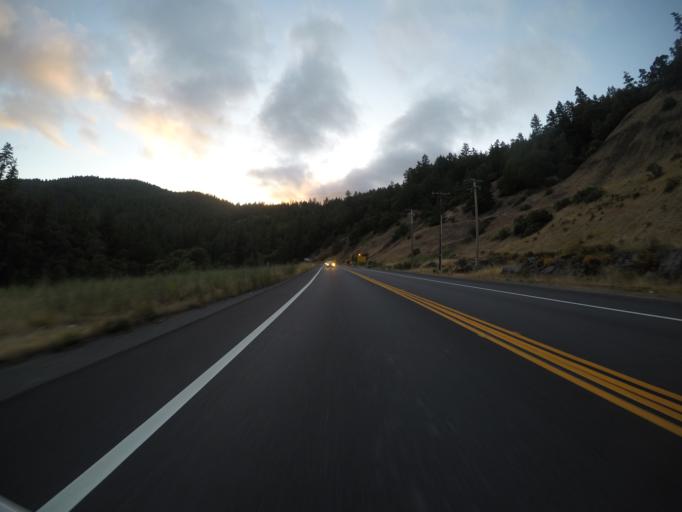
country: US
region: California
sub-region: Humboldt County
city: Redway
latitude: 40.0344
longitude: -123.7861
